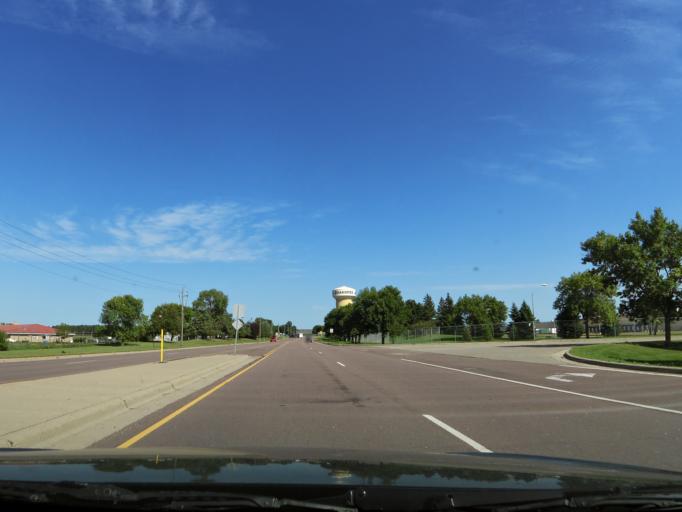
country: US
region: Minnesota
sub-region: Scott County
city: Shakopee
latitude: 44.7869
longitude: -93.4697
